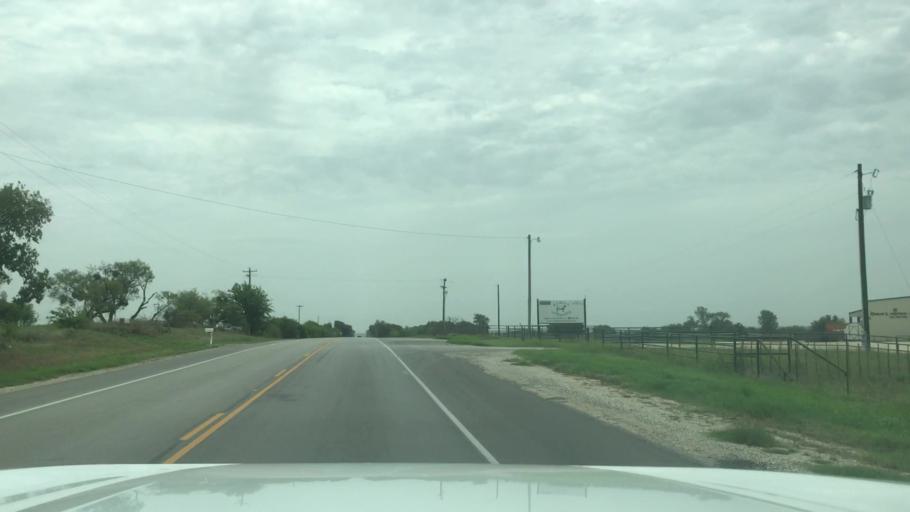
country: US
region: Texas
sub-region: Erath County
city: Dublin
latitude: 32.0867
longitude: -98.2559
